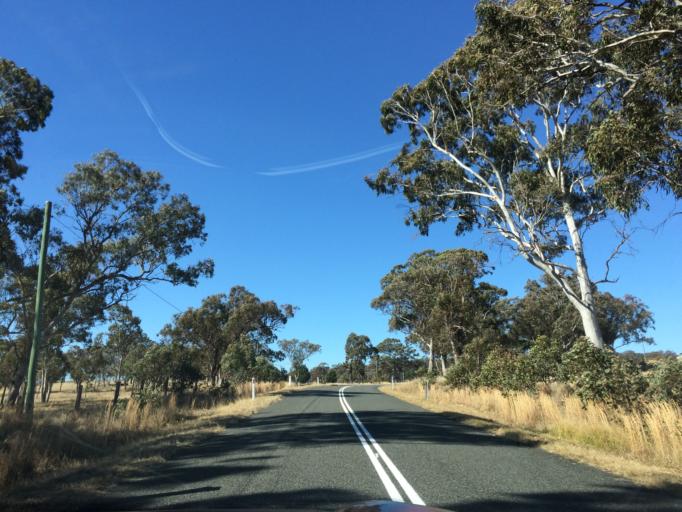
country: AU
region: Queensland
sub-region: Southern Downs
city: Stanthorpe
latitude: -28.6956
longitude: 152.0122
